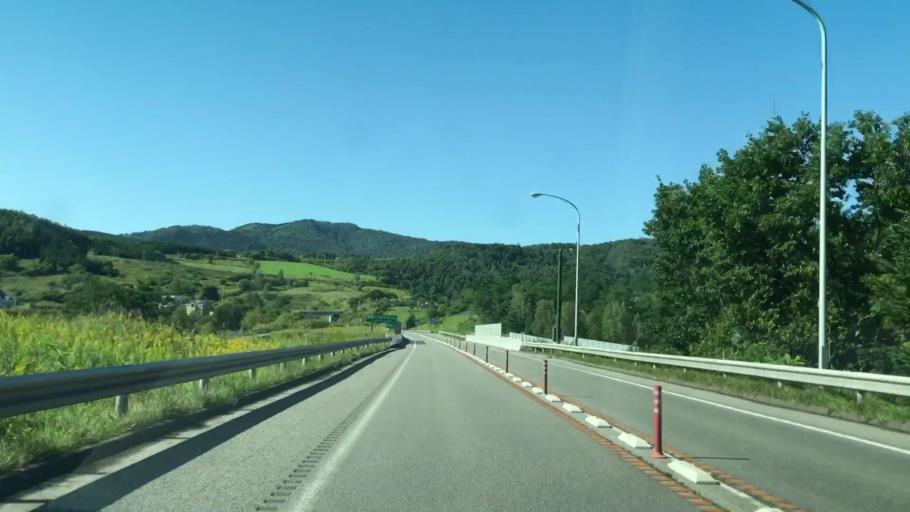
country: JP
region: Hokkaido
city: Date
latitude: 42.5470
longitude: 140.7921
